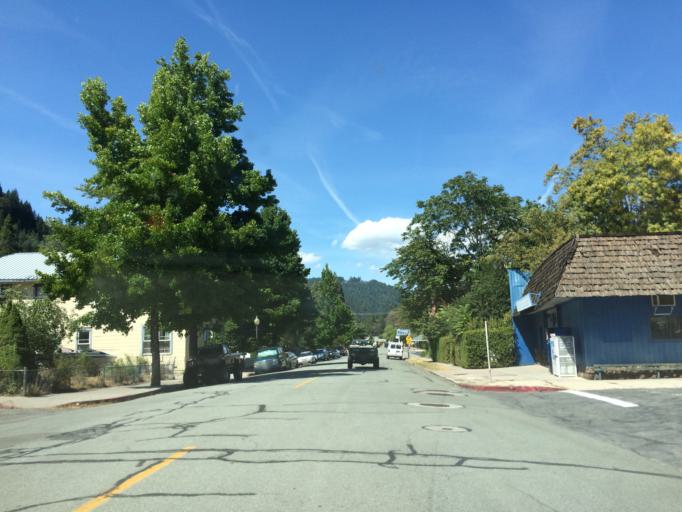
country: US
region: California
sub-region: Siskiyou County
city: Dunsmuir
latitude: 41.2142
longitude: -122.2722
